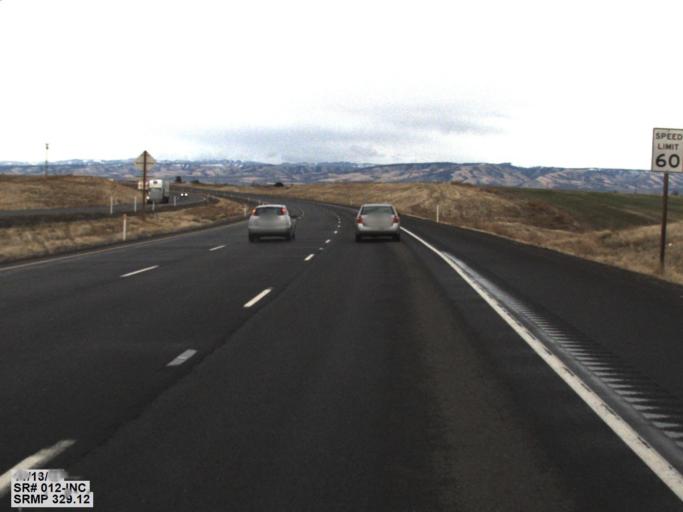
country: US
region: Washington
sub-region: Walla Walla County
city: Garrett
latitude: 46.0487
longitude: -118.4886
